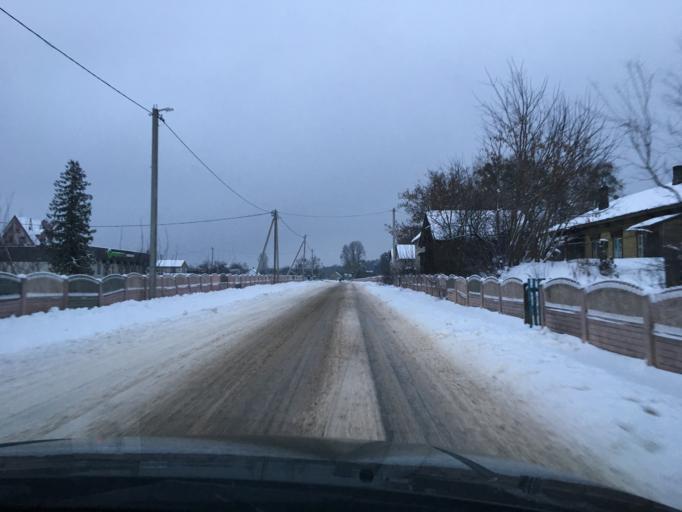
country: LT
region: Alytaus apskritis
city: Druskininkai
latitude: 53.8845
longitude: 24.1342
